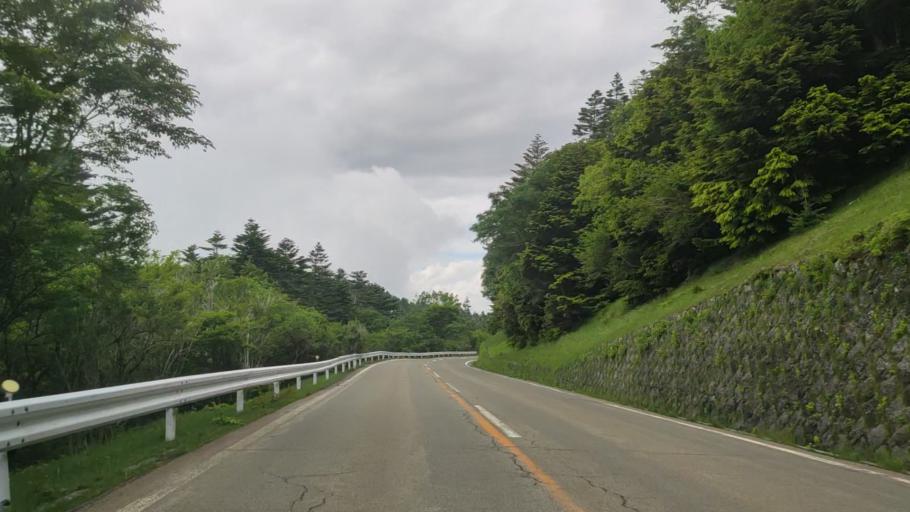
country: JP
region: Yamanashi
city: Fujikawaguchiko
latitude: 35.3957
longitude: 138.6920
